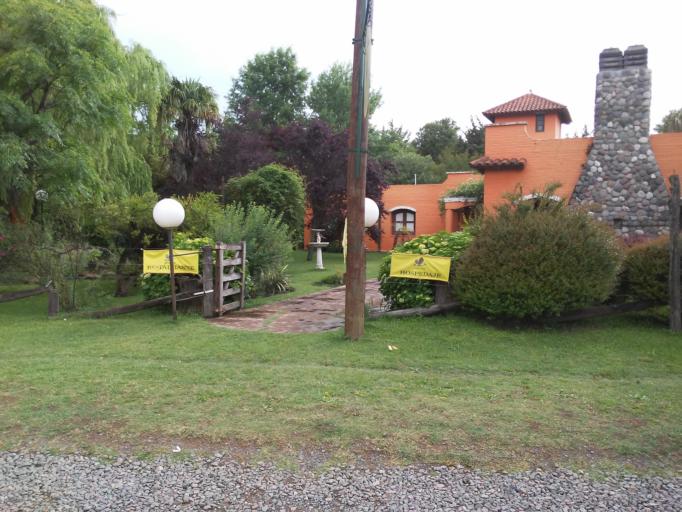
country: AR
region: Buenos Aires
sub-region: Partido de Mercedes
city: Mercedes
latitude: -34.7005
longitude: -59.3189
